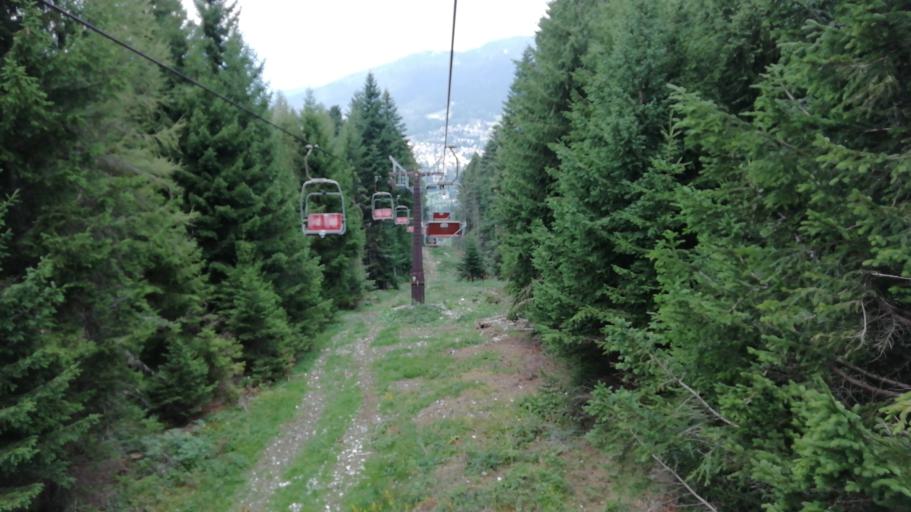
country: IT
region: Trentino-Alto Adige
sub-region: Provincia di Trento
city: Folgaria
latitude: 45.8977
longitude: 11.1932
